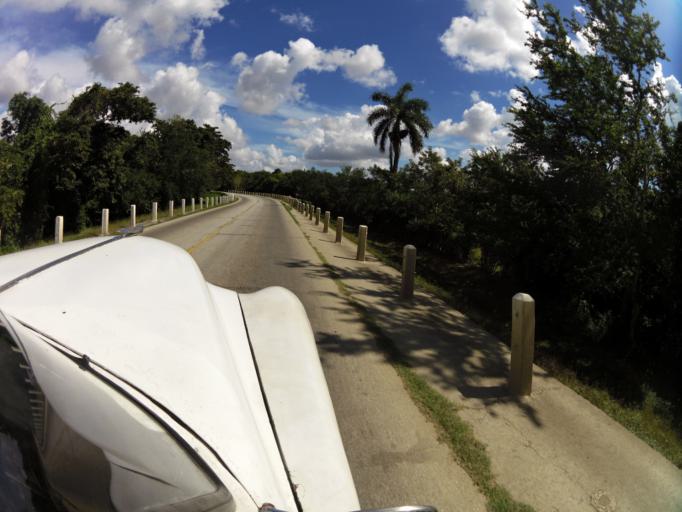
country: CU
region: Holguin
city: Cacocum
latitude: 20.8640
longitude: -76.4397
